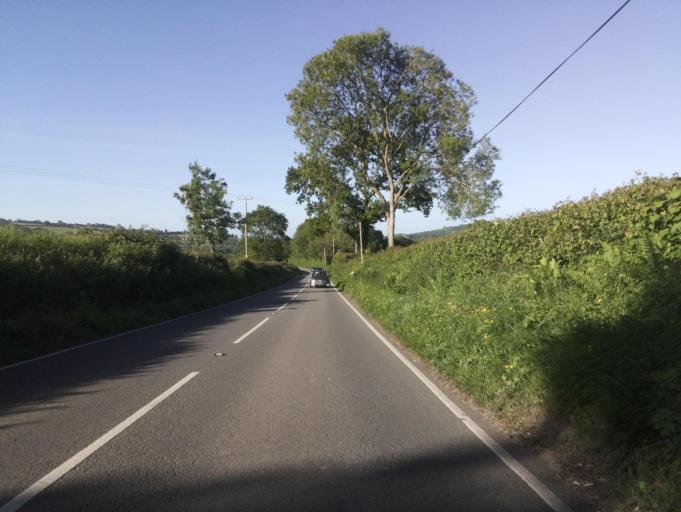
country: GB
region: England
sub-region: Somerset
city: Crewkerne
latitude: 50.8422
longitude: -2.8530
